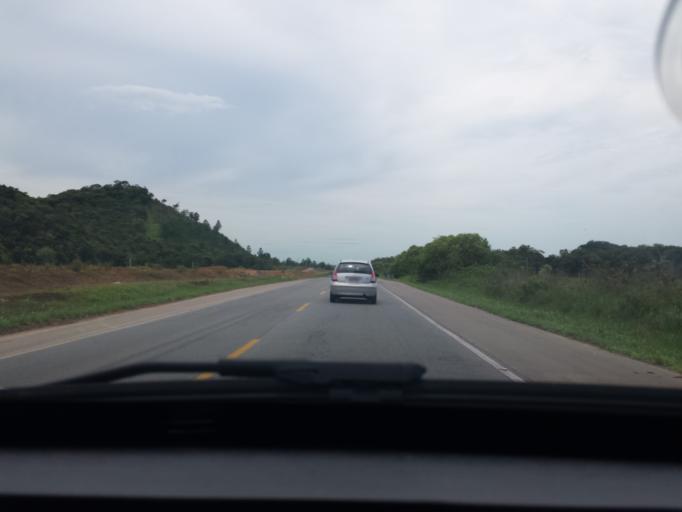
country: BR
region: Santa Catarina
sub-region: Gaspar
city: Gaspar
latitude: -26.8814
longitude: -48.8515
